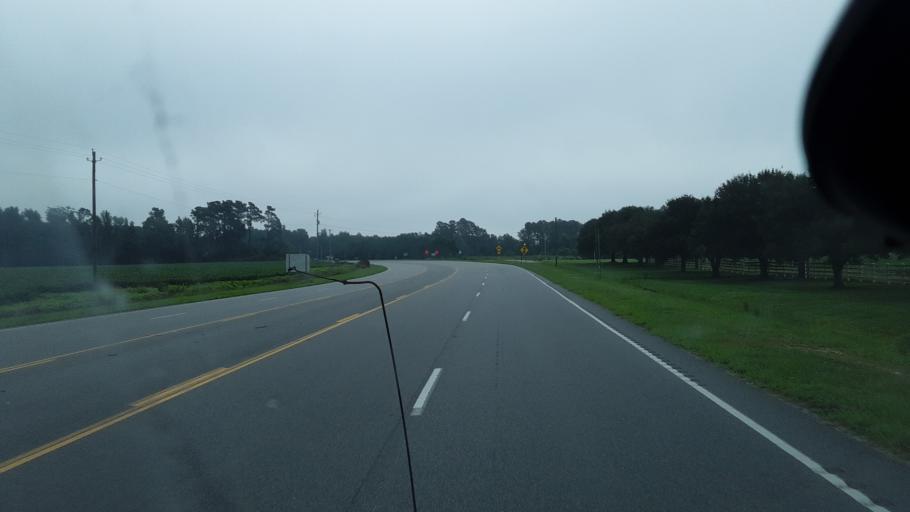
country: US
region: South Carolina
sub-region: Florence County
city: Johnsonville
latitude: 33.8818
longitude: -79.4583
